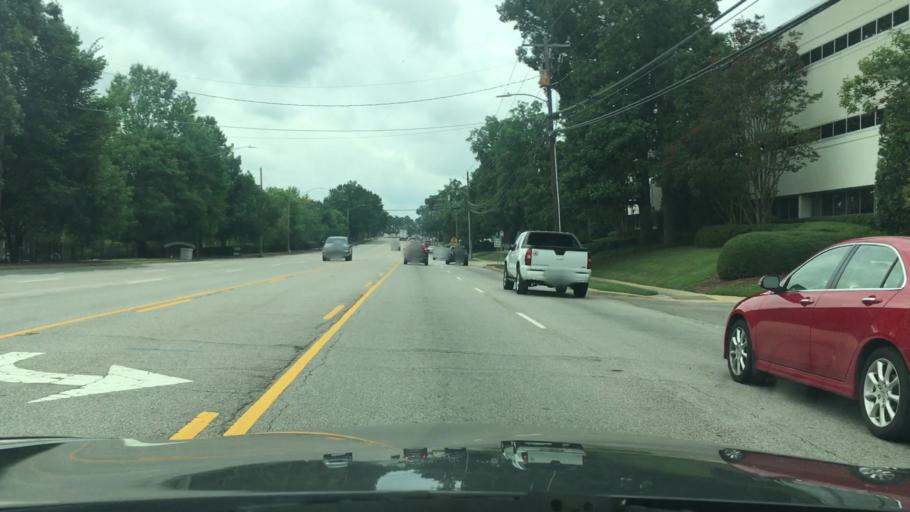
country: US
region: North Carolina
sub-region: Wake County
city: West Raleigh
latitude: 35.8596
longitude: -78.6392
